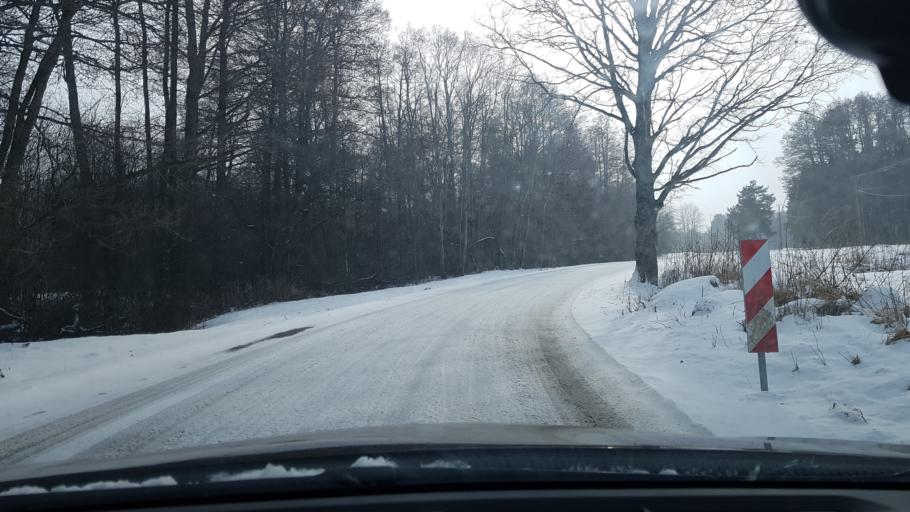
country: EE
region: Harju
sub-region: Kuusalu vald
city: Kuusalu
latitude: 59.4818
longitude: 25.4126
